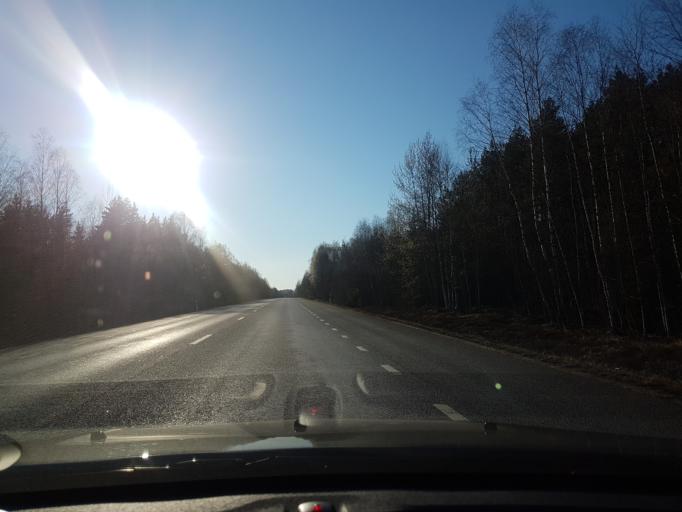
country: SE
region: Uppsala
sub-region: Heby Kommun
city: Morgongava
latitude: 59.8948
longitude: 17.1331
